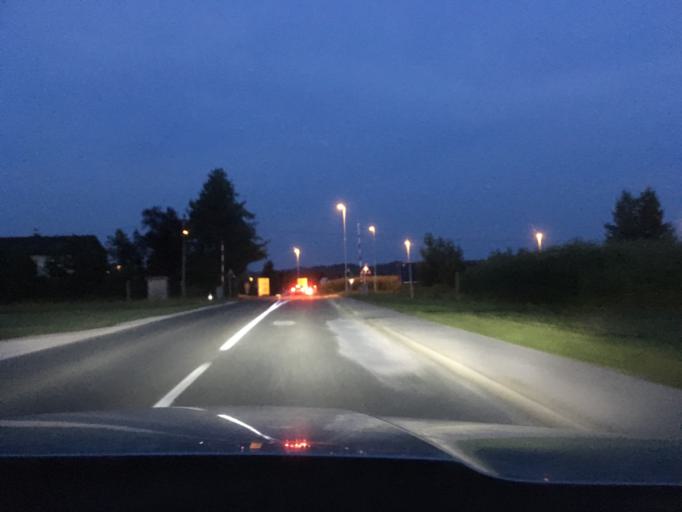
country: SI
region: Kamnik
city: Smarca
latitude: 46.1987
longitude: 14.5904
